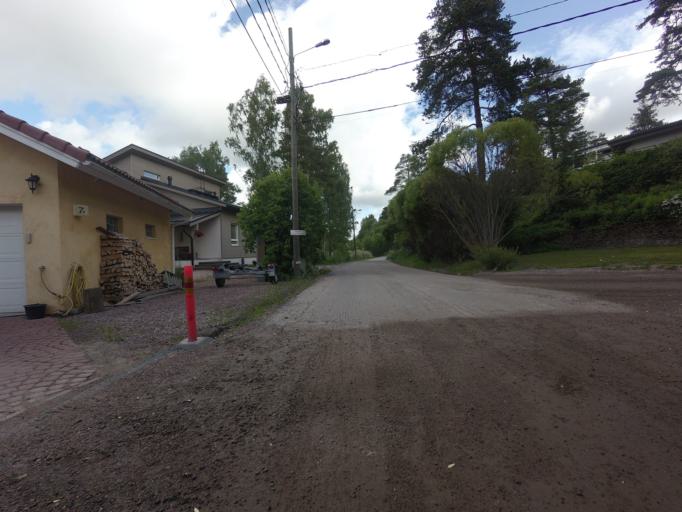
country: FI
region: Uusimaa
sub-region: Helsinki
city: Espoo
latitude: 60.1650
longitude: 24.5968
